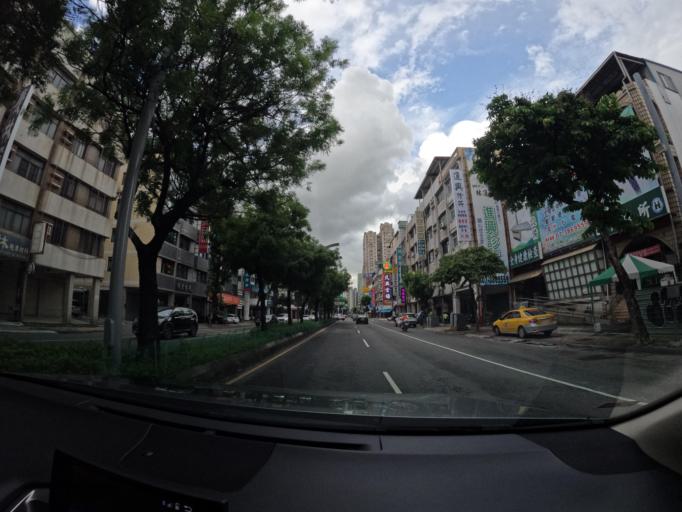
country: TW
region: Taiwan
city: Fengshan
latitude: 22.6369
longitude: 120.3393
